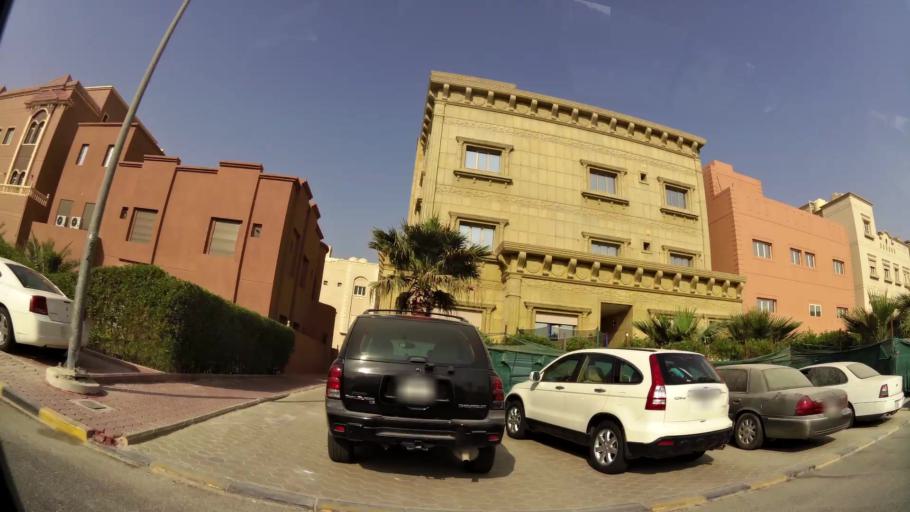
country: KW
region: Al Asimah
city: Ar Rabiyah
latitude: 29.2993
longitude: 47.8114
